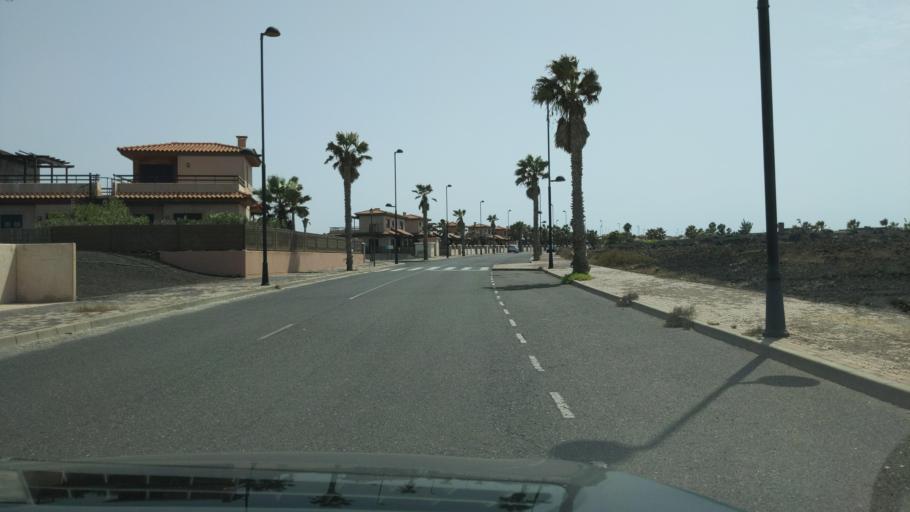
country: ES
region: Canary Islands
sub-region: Provincia de Las Palmas
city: Corralejo
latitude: 28.7327
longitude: -13.9459
